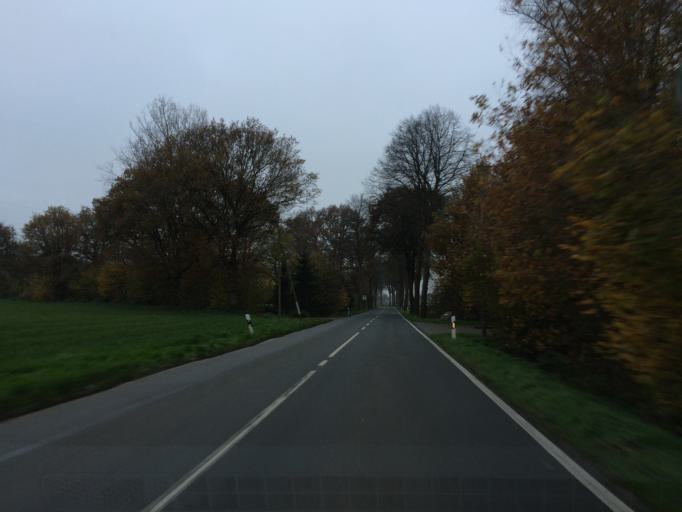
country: DE
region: North Rhine-Westphalia
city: Marl
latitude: 51.6993
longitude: 7.0606
